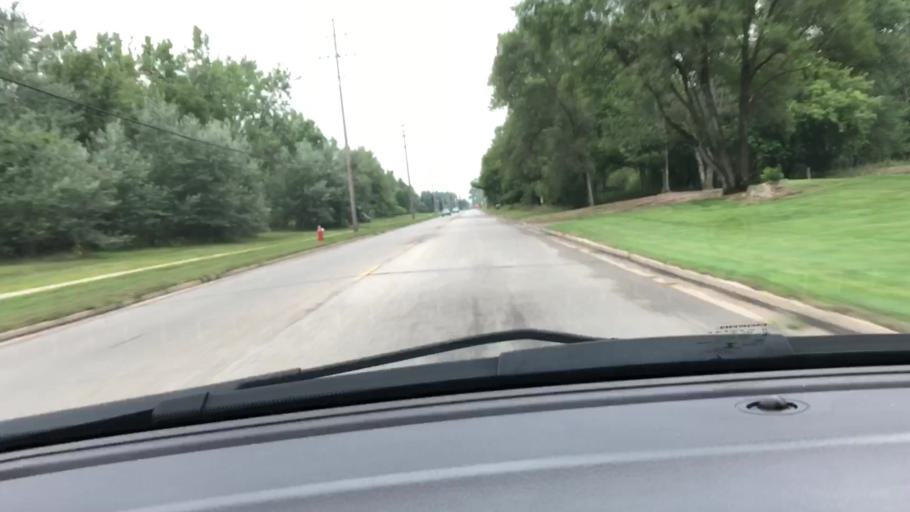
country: US
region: Michigan
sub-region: Midland County
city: Midland
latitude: 43.6176
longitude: -84.1874
